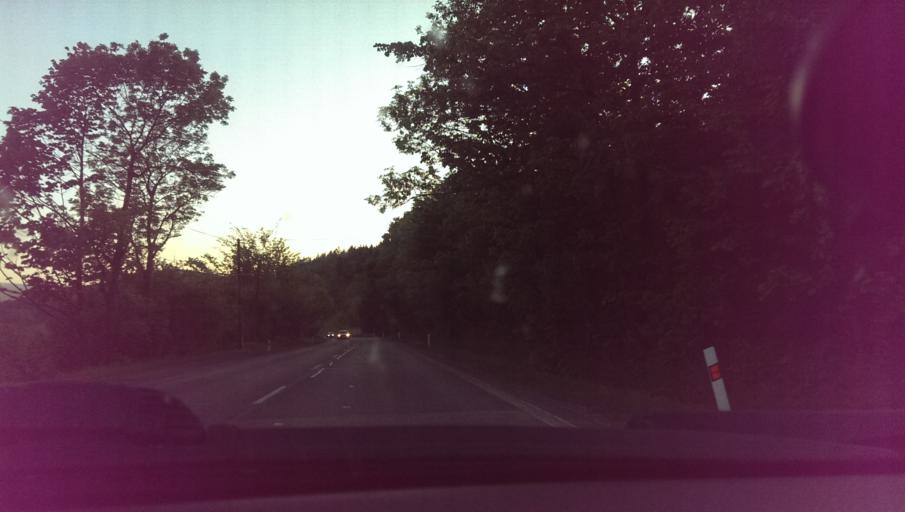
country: CZ
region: Zlin
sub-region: Okres Vsetin
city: Dolni Becva
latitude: 49.4942
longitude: 18.1756
